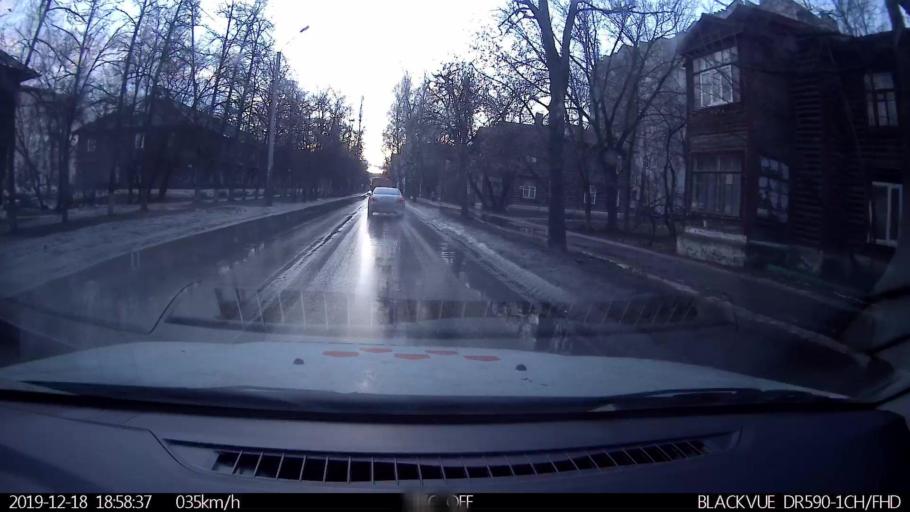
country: RU
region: Nizjnij Novgorod
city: Gorbatovka
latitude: 56.3347
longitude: 43.8399
